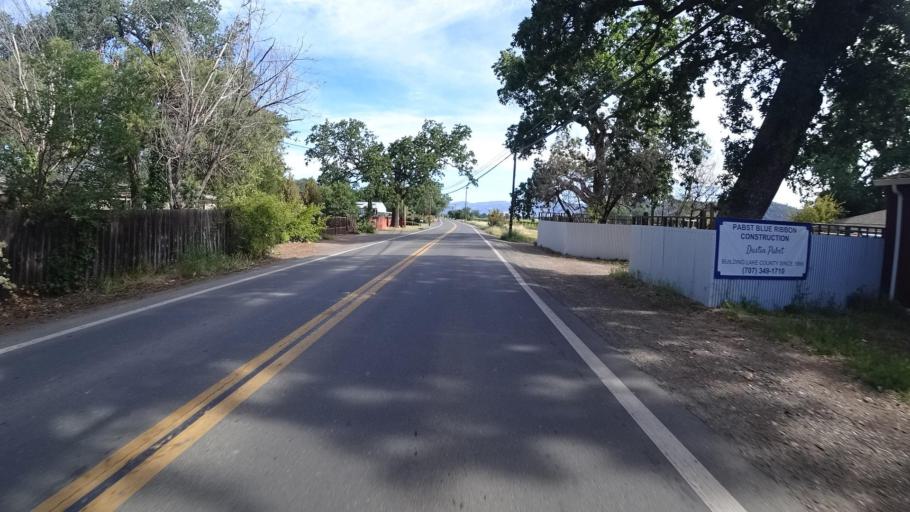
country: US
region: California
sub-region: Lake County
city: Kelseyville
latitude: 38.9825
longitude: -122.8292
